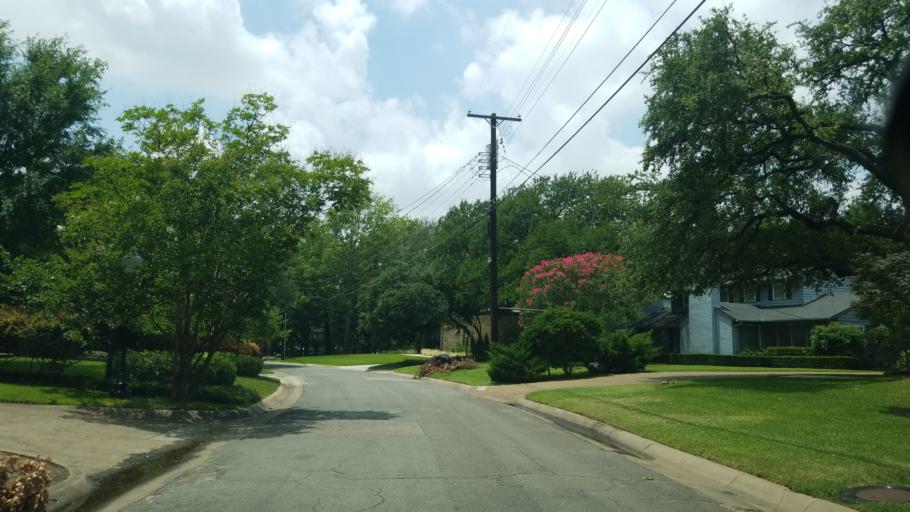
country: US
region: Texas
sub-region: Dallas County
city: University Park
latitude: 32.8379
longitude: -96.8163
